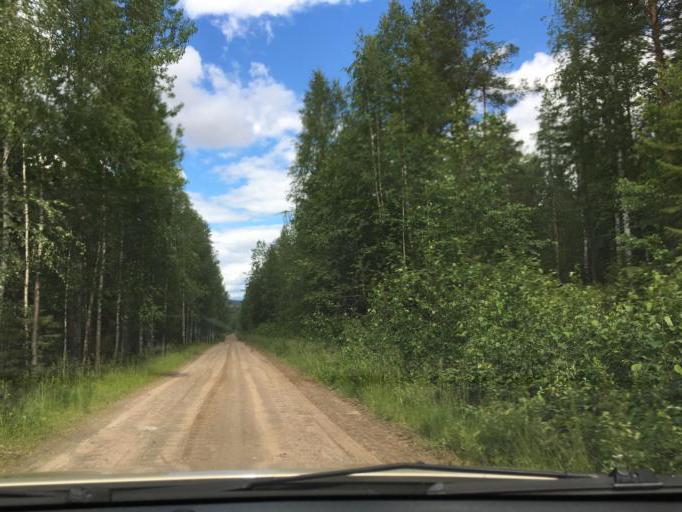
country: SE
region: Norrbotten
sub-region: Overkalix Kommun
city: OEverkalix
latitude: 66.1357
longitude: 22.7842
